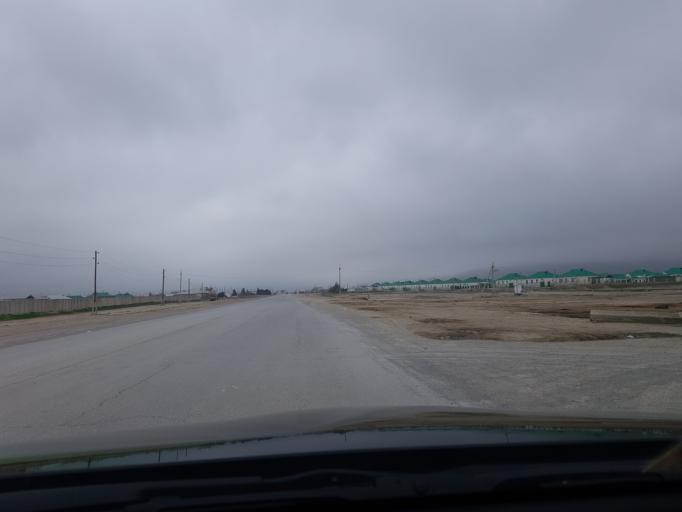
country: TM
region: Ahal
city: Arcabil
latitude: 38.1326
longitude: 57.9463
